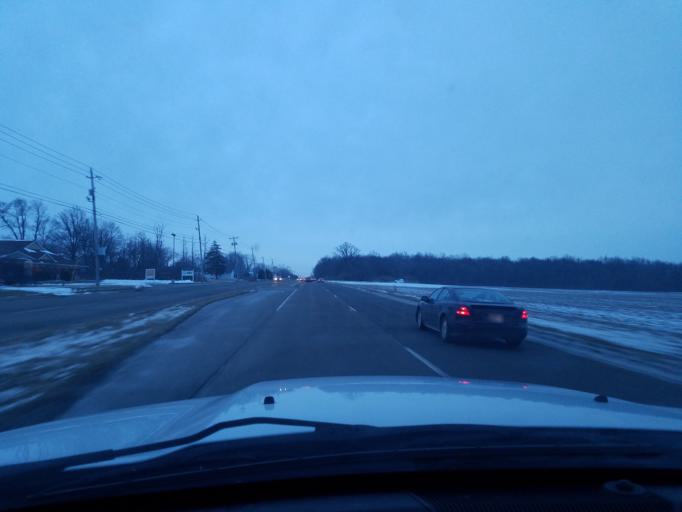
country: US
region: Indiana
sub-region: Delaware County
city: Muncie
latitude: 40.2191
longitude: -85.3562
